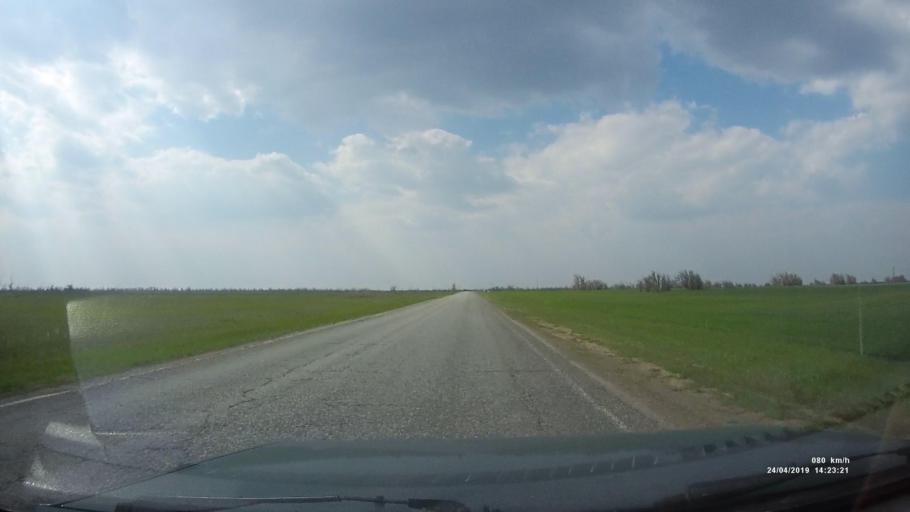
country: RU
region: Kalmykiya
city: Arshan'
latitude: 46.3218
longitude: 44.1148
